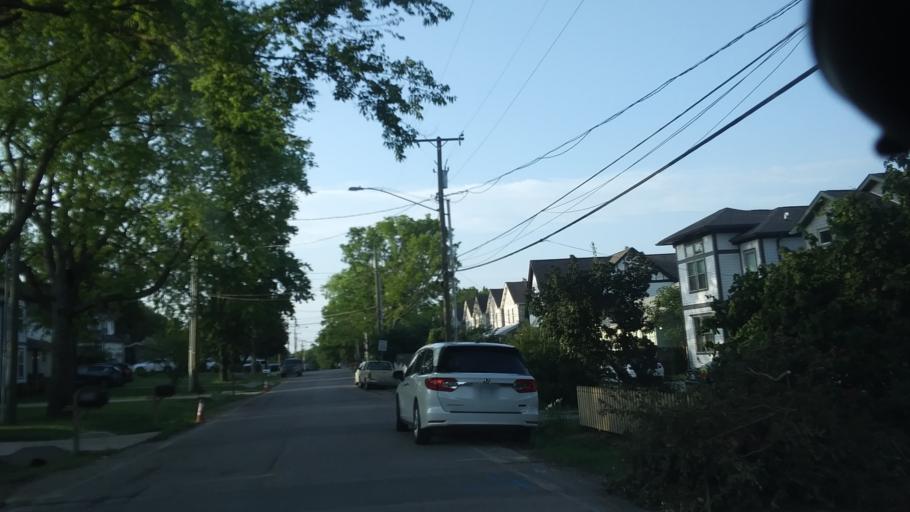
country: US
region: Tennessee
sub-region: Davidson County
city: Belle Meade
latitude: 36.1590
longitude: -86.8732
